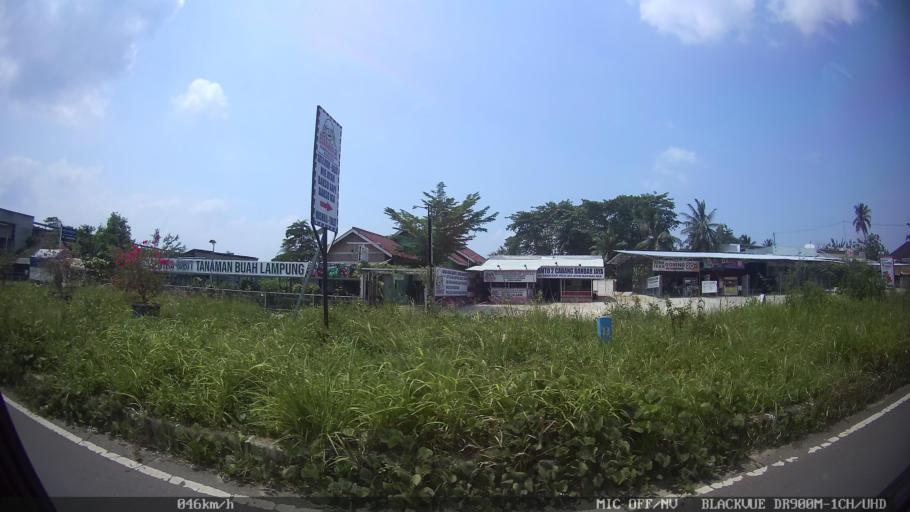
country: ID
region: Lampung
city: Kedaton
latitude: -5.3531
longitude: 105.3223
